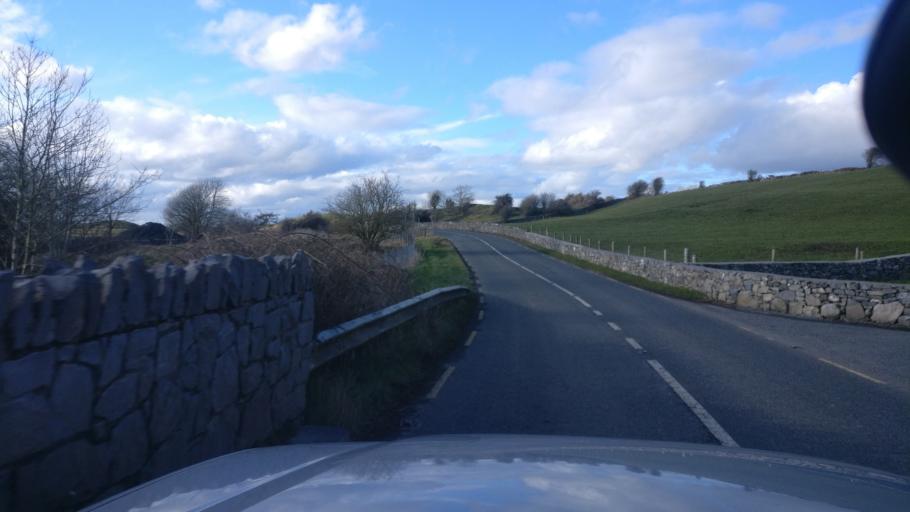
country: IE
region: Connaught
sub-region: County Galway
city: Loughrea
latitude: 53.1886
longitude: -8.3899
